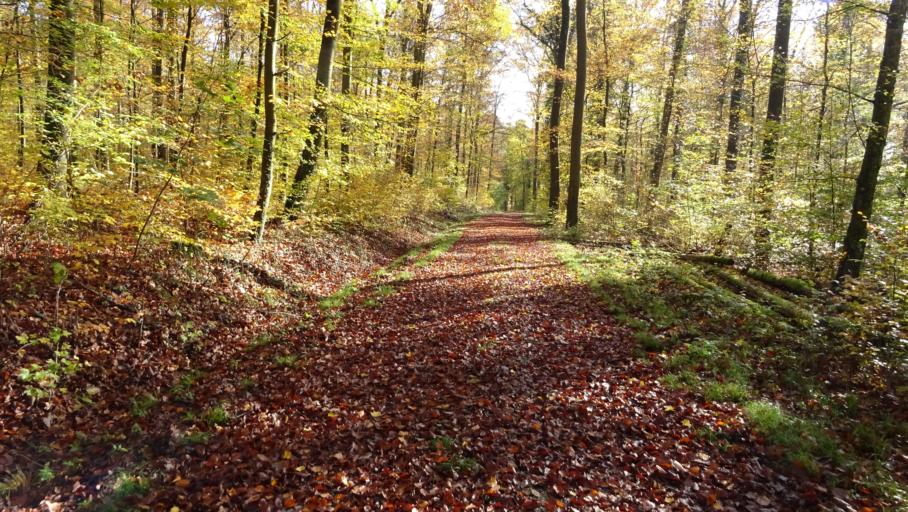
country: DE
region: Baden-Wuerttemberg
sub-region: Karlsruhe Region
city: Obrigheim
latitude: 49.3717
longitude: 9.0976
